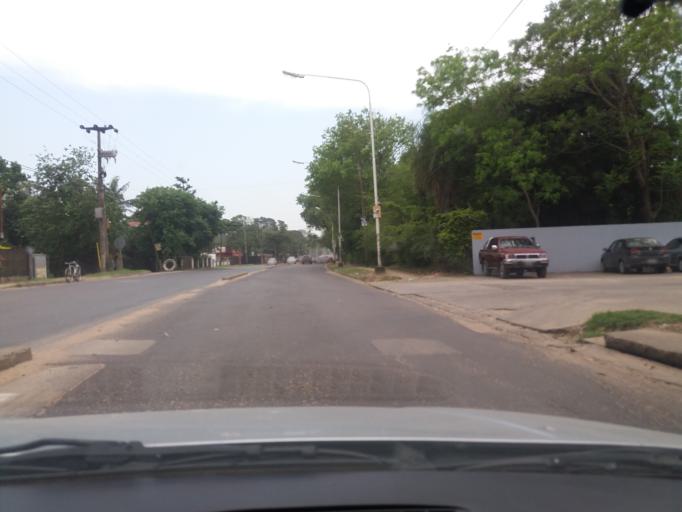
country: AR
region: Corrientes
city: Corrientes
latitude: -27.5099
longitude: -58.8101
